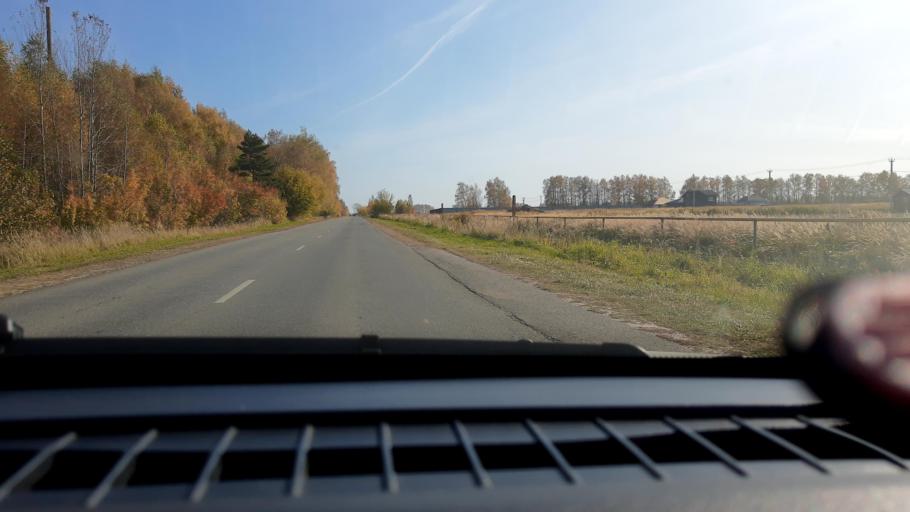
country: RU
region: Nizjnij Novgorod
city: Kstovo
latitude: 56.1544
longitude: 44.2773
